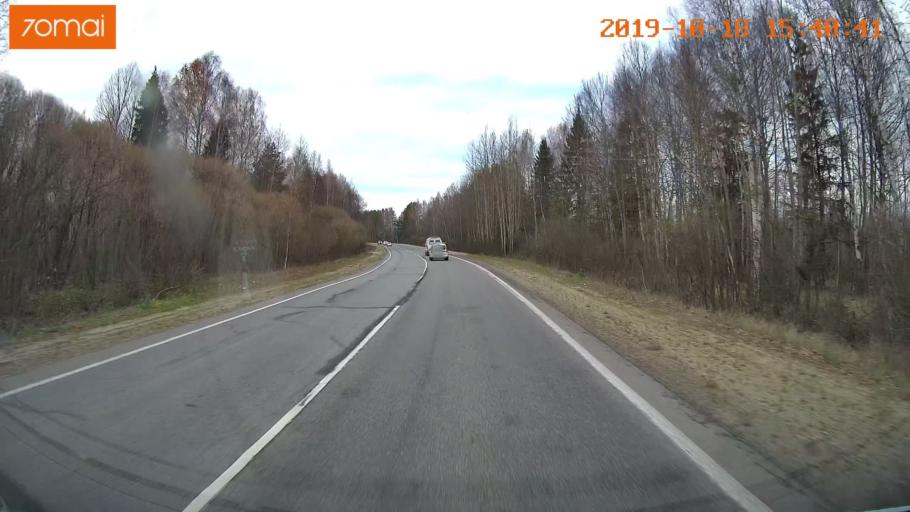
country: RU
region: Vladimir
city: Golovino
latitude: 55.9373
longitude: 40.5923
